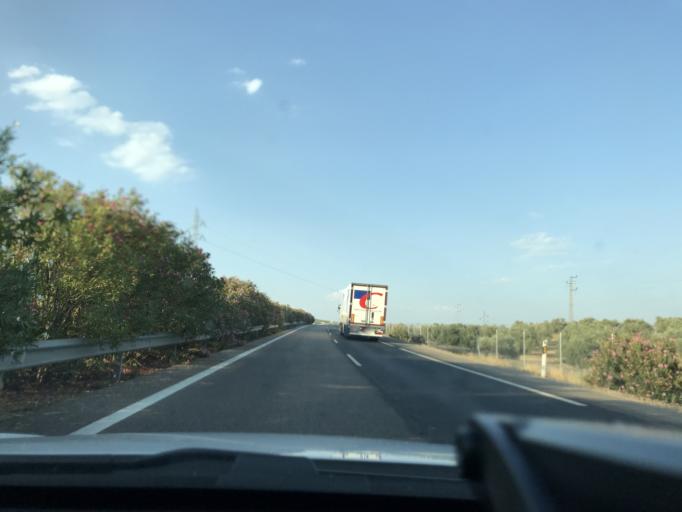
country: ES
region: Andalusia
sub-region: Provincia de Jaen
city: Espeluy
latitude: 38.0599
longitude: -3.8915
